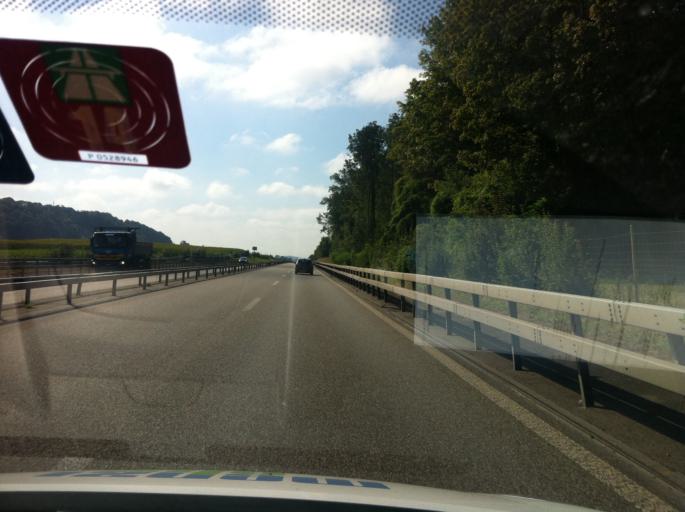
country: CH
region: Zurich
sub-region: Bezirk Buelach
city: Bachenbulach
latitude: 47.4948
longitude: 8.5383
